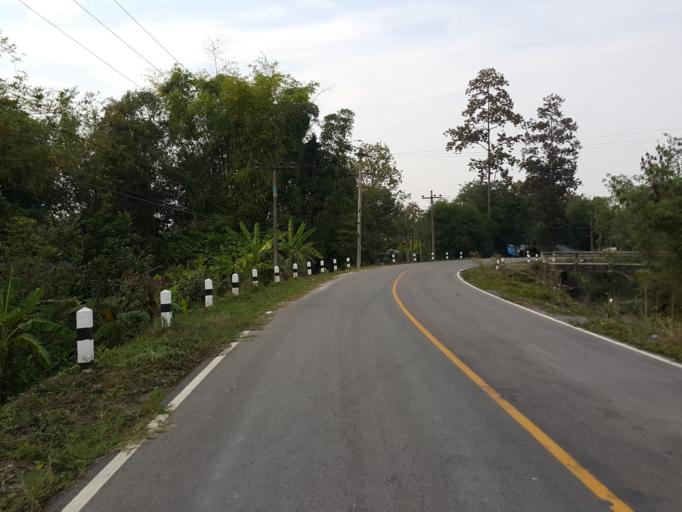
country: TH
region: Chiang Mai
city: San Kamphaeng
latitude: 18.8433
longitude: 99.1517
